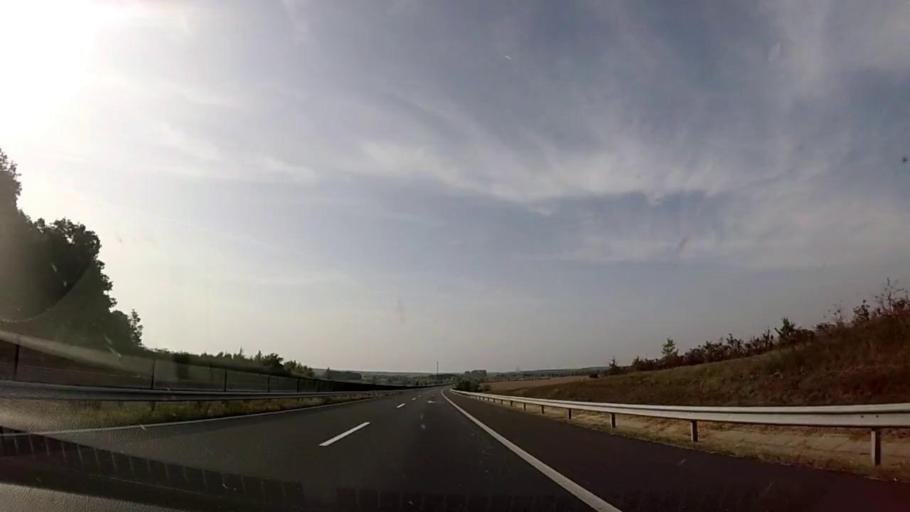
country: HU
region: Somogy
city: Balatonbereny
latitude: 46.6555
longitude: 17.3084
